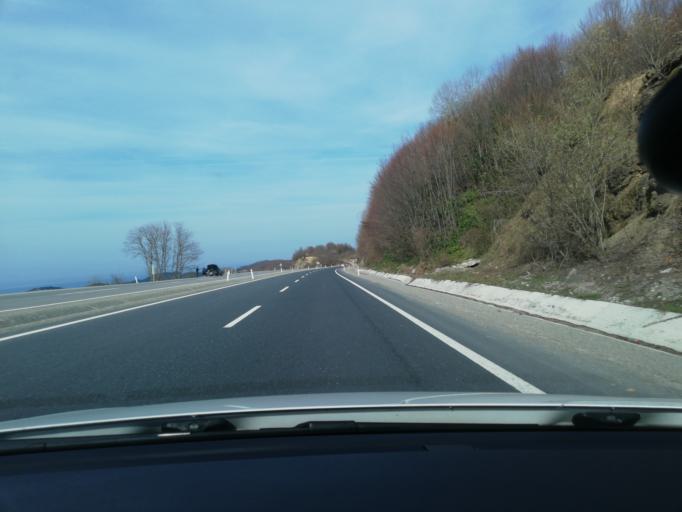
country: TR
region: Zonguldak
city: Kozlu
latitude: 41.3415
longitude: 31.6298
